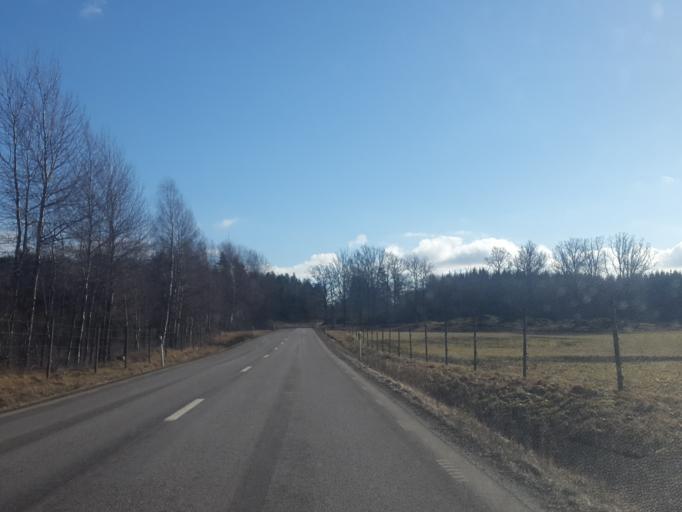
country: SE
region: Vaestra Goetaland
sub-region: Alingsas Kommun
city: Alingsas
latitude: 57.9609
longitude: 12.4471
